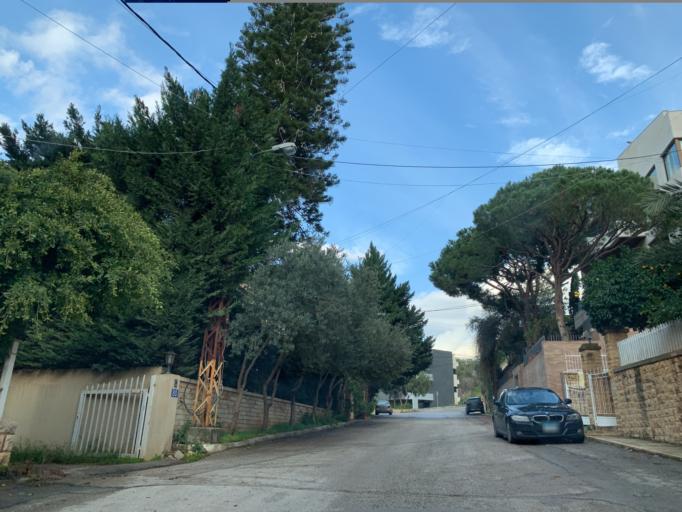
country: LB
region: Mont-Liban
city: Baabda
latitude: 33.8515
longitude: 35.5766
